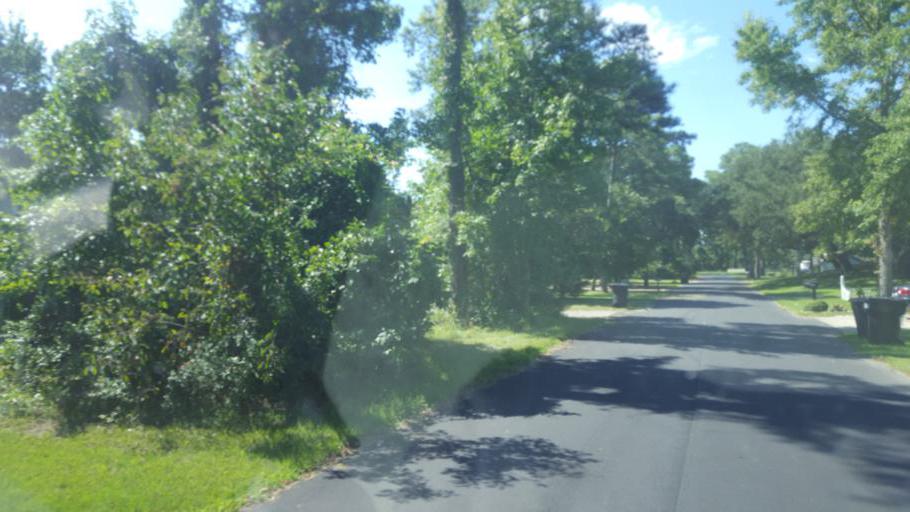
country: US
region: North Carolina
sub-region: Dare County
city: Kill Devil Hills
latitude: 36.0083
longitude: -75.6778
